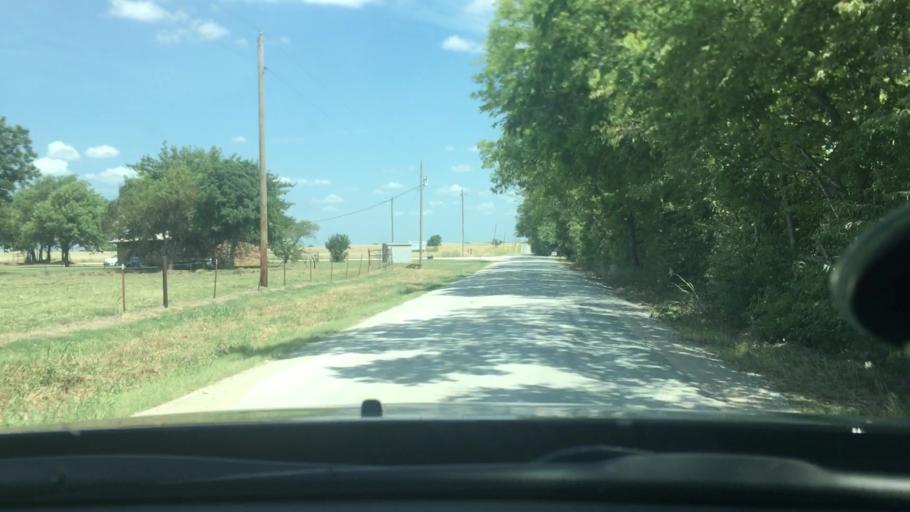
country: US
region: Oklahoma
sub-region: Love County
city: Marietta
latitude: 33.9828
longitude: -97.1870
